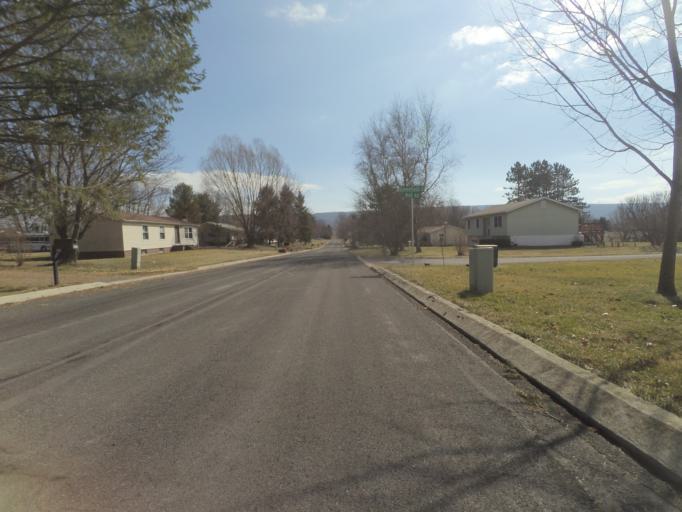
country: US
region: Pennsylvania
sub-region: Centre County
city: Pine Grove Mills
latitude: 40.7326
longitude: -77.9333
